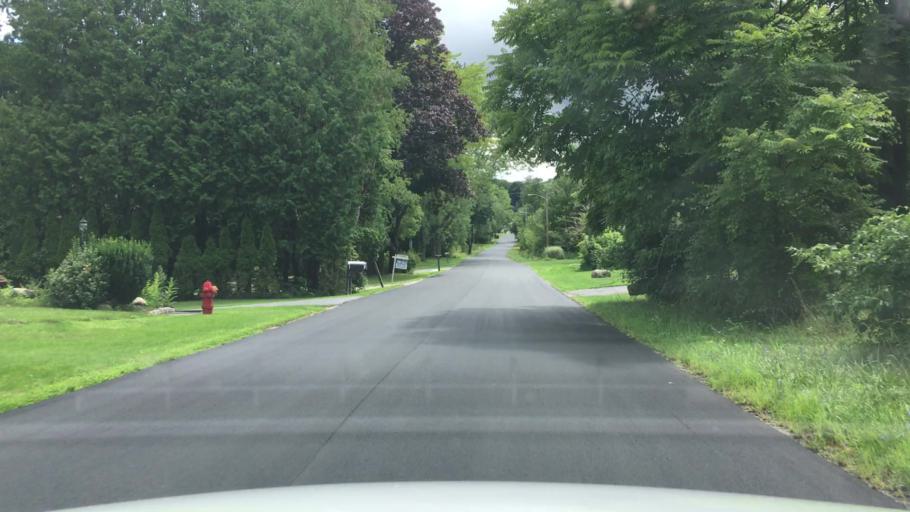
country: US
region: Vermont
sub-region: Bennington County
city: Bennington
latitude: 42.8868
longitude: -73.2069
